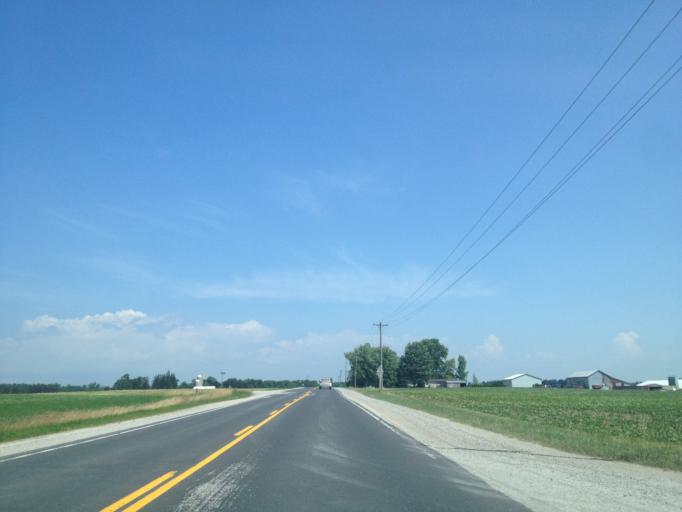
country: CA
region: Ontario
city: Stratford
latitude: 43.3647
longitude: -81.2116
